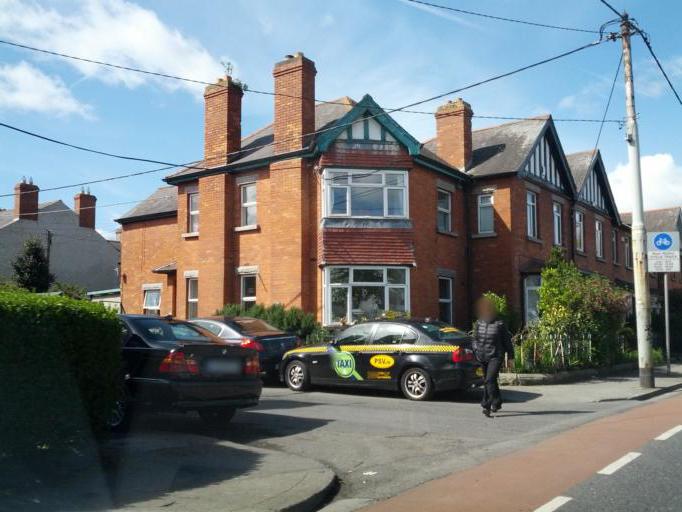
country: IE
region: Leinster
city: Rathgar
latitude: 53.3301
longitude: -6.2814
